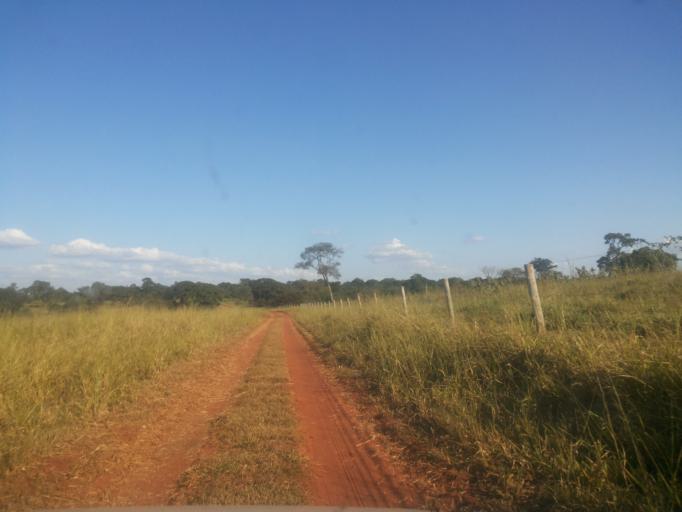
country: BR
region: Minas Gerais
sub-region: Santa Vitoria
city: Santa Vitoria
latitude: -19.0076
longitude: -50.4538
